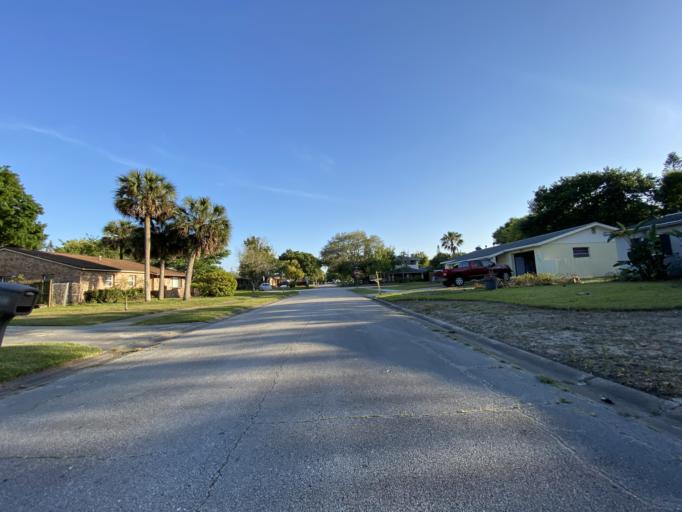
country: US
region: Florida
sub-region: Volusia County
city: South Daytona
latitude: 29.1774
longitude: -81.0120
